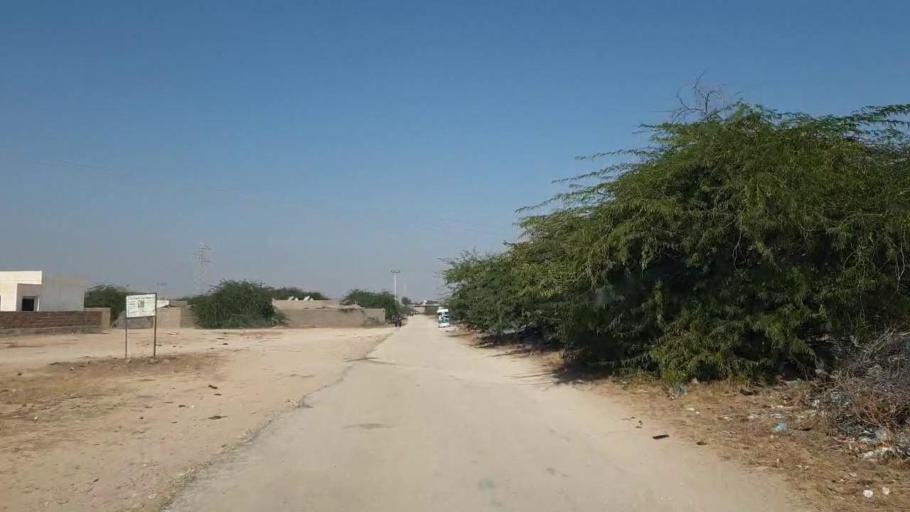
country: PK
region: Sindh
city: Jamshoro
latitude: 25.3530
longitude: 67.8312
